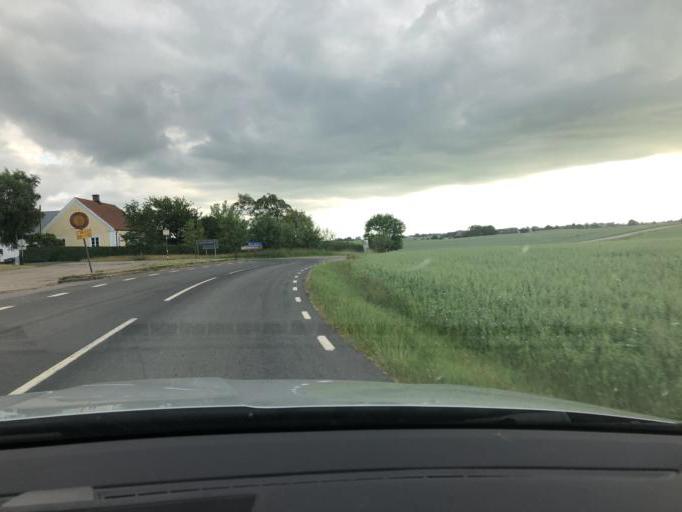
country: SE
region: Skane
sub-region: Simrishamns Kommun
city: Simrishamn
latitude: 55.5129
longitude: 14.2381
